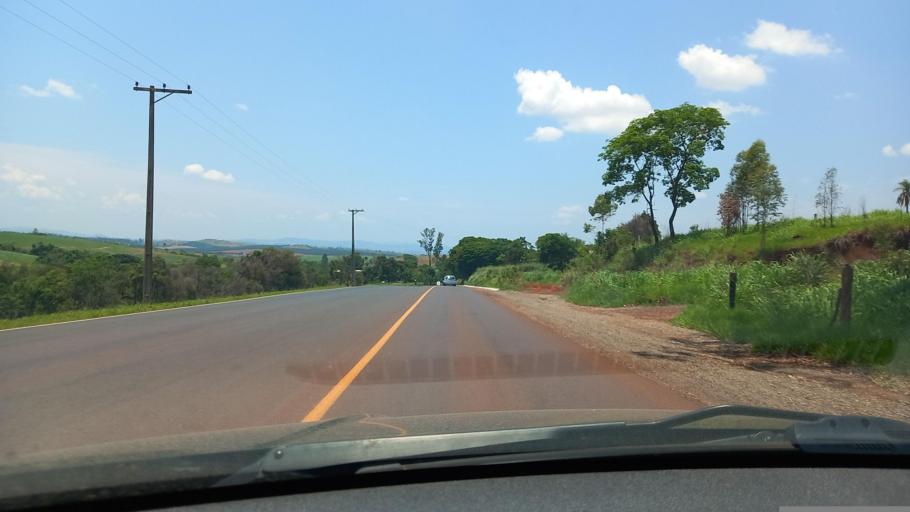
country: BR
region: Sao Paulo
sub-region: Moji-Guacu
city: Mogi-Gaucu
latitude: -22.3440
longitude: -46.8799
